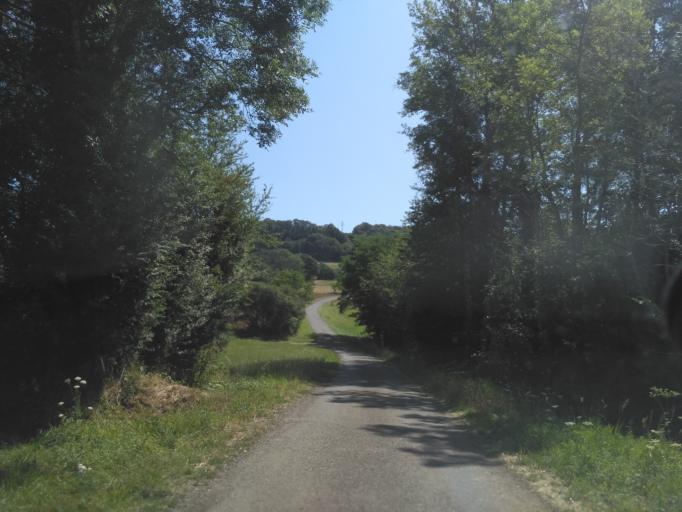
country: FR
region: Franche-Comte
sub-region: Departement de la Haute-Saone
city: Villersexel
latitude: 47.5072
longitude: 6.5223
